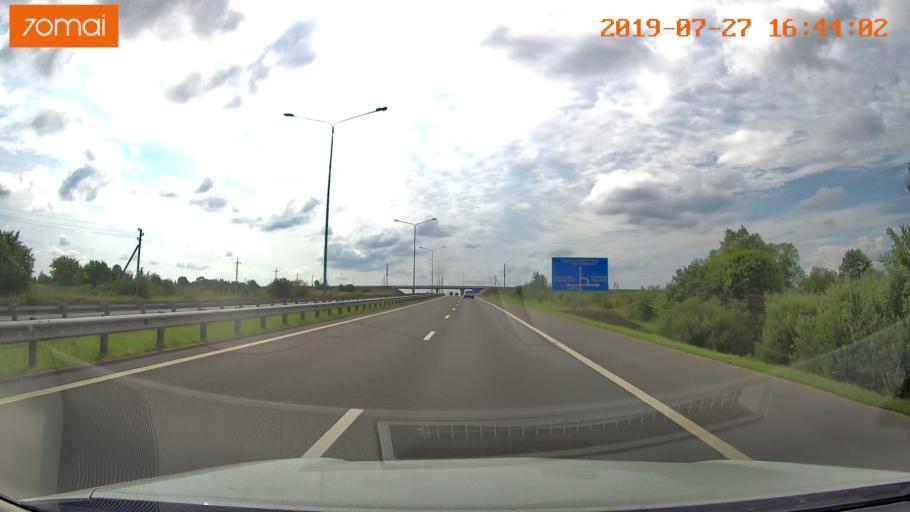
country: RU
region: Kaliningrad
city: Gvardeysk
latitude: 54.6724
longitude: 21.0870
